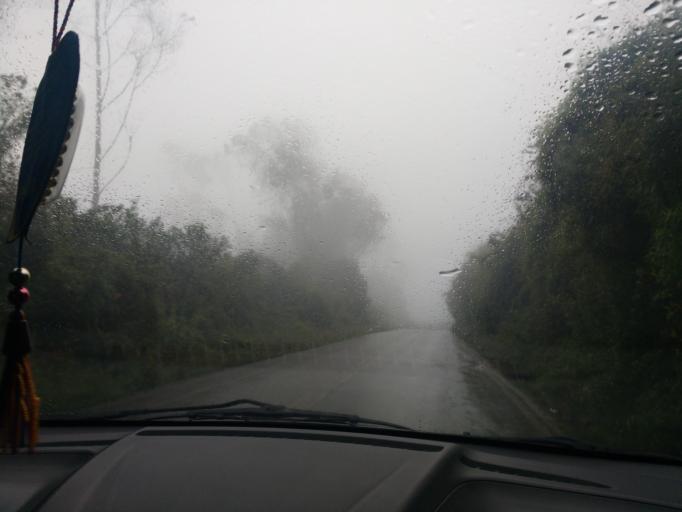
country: CO
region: Bogota D.C.
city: Bogota
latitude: 4.5874
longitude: -74.0258
